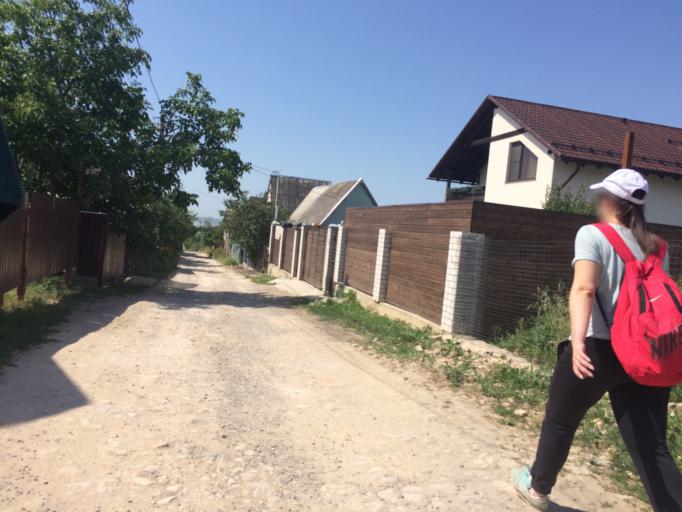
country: RU
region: Stavropol'skiy
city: Tatarka
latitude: 44.9843
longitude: 41.9417
